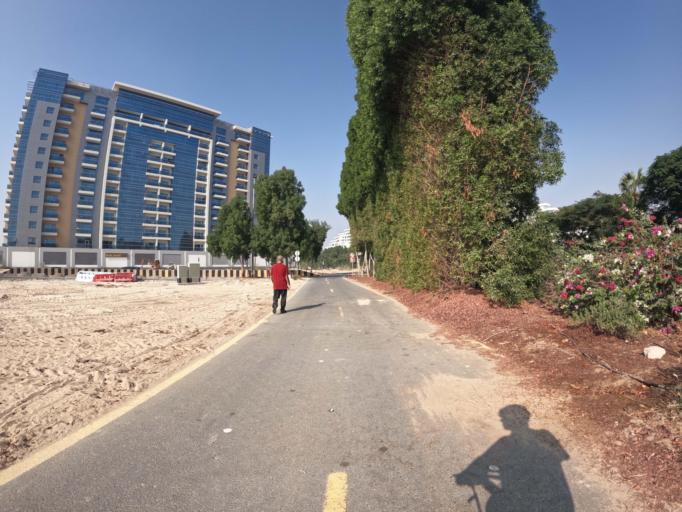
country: AE
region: Dubai
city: Dubai
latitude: 25.0974
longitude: 55.3186
